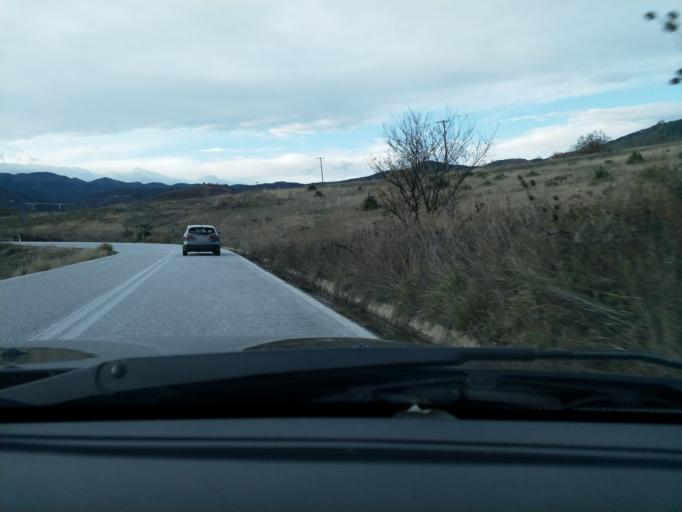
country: GR
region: Epirus
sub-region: Nomos Ioanninon
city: Metsovo
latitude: 39.7966
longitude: 21.3649
